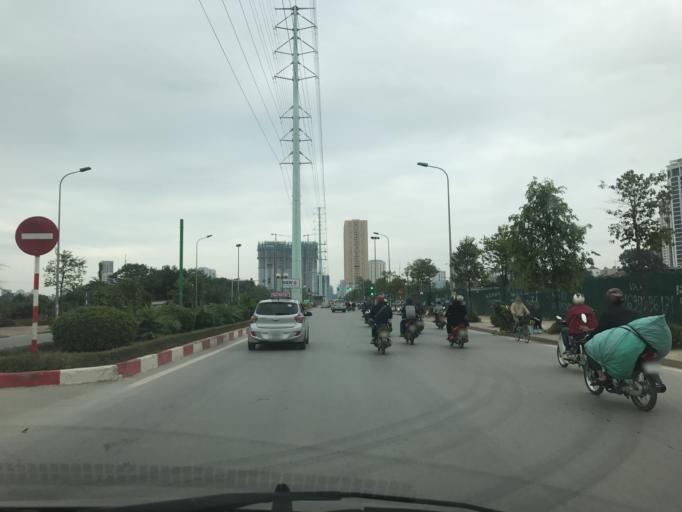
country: VN
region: Ha Noi
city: Ha Dong
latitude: 20.9866
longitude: 105.7776
